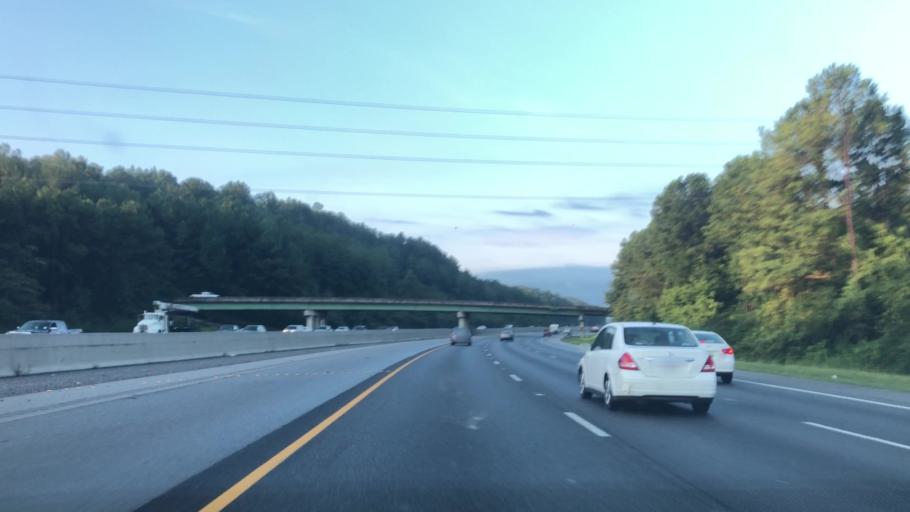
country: US
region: Alabama
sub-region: Shelby County
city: Pelham
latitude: 33.3107
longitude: -86.7871
